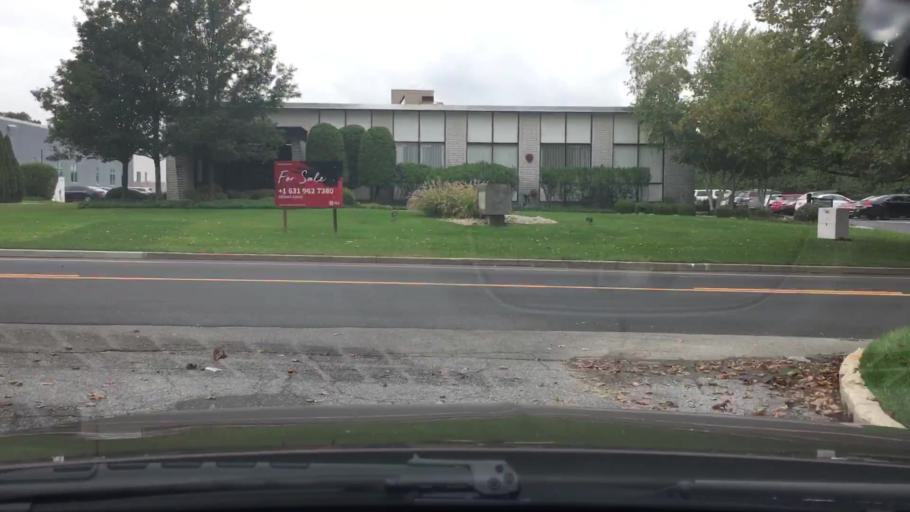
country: US
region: New York
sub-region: Suffolk County
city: Brentwood
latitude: 40.8162
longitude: -73.2472
